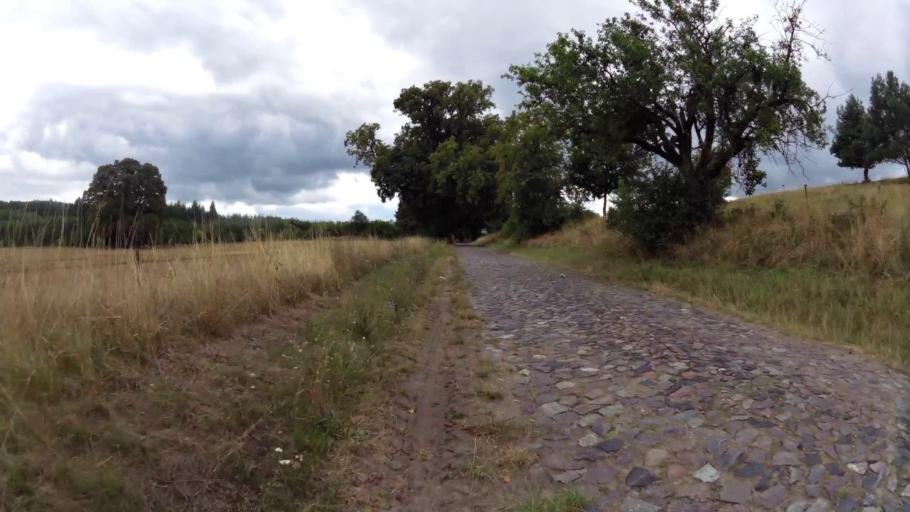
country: PL
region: West Pomeranian Voivodeship
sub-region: Powiat mysliborski
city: Debno
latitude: 52.8265
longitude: 14.7239
